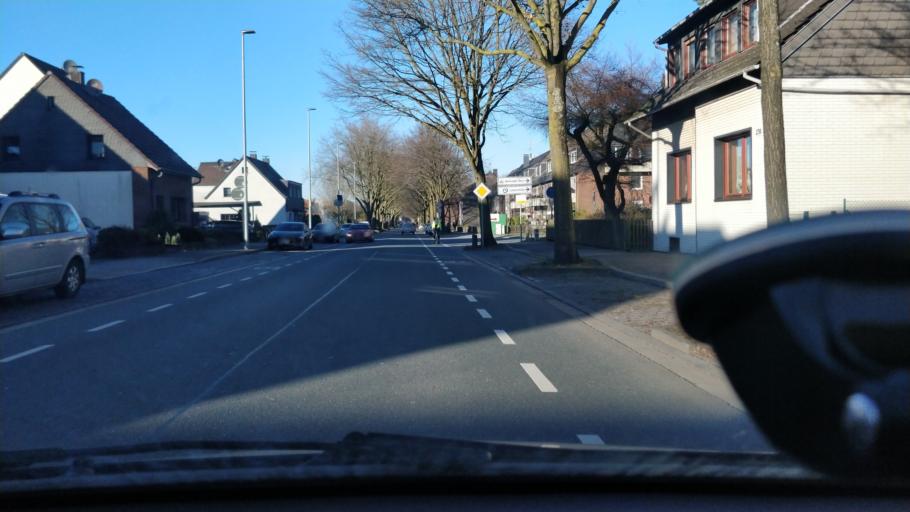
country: DE
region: North Rhine-Westphalia
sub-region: Regierungsbezirk Munster
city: Bottrop
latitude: 51.5432
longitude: 6.8666
